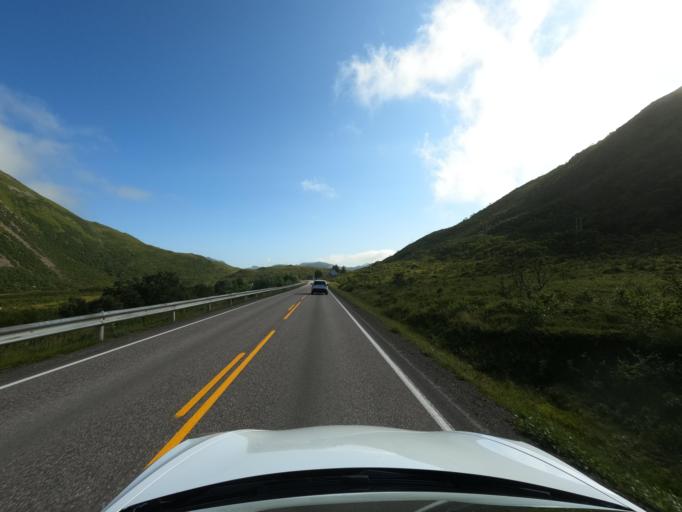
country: NO
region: Nordland
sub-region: Vestvagoy
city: Evjen
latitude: 68.2713
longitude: 13.8330
